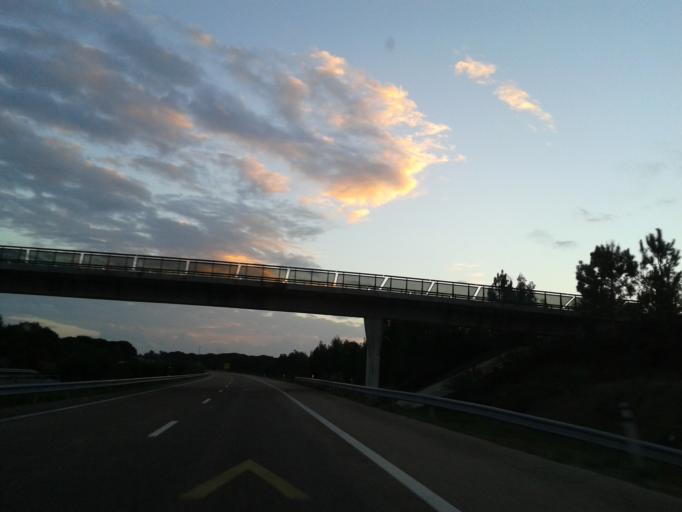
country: PT
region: Evora
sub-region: Vendas Novas
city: Vendas Novas
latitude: 38.6586
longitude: -8.6615
